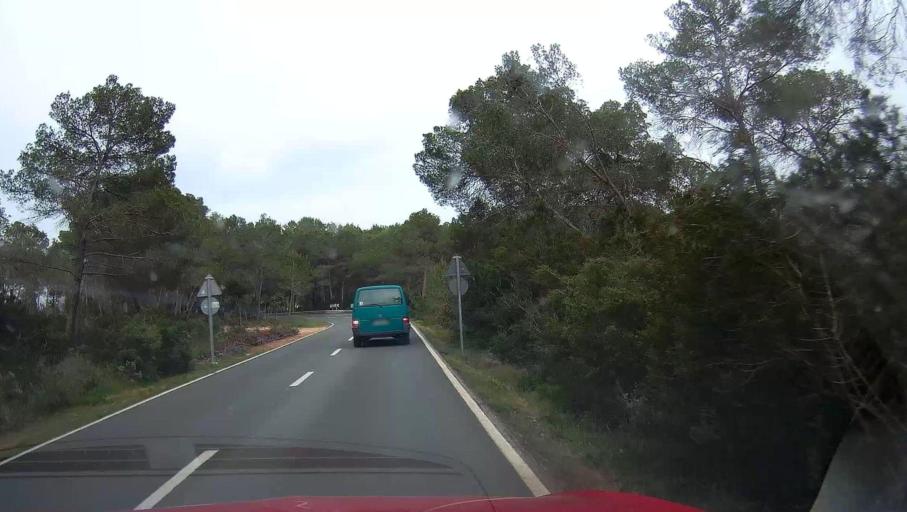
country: ES
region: Balearic Islands
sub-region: Illes Balears
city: Sant Joan de Labritja
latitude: 39.0471
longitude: 1.4095
